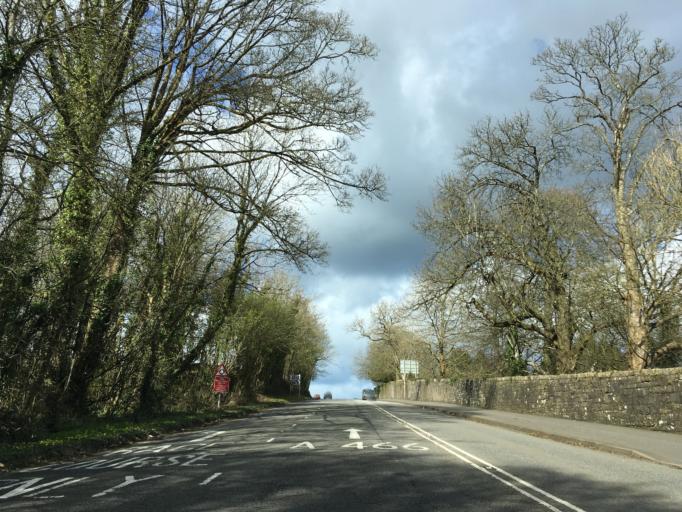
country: GB
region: Wales
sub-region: Monmouthshire
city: Chepstow
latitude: 51.6486
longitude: -2.6908
